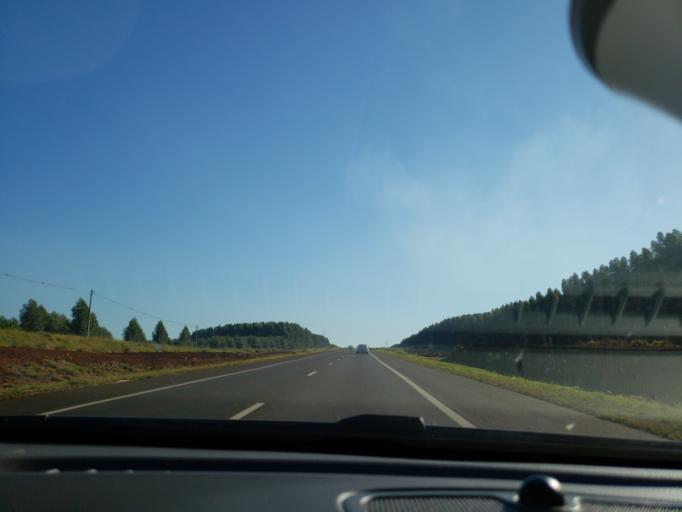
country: AR
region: Misiones
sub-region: Departamento de Capital
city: Posadas
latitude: -27.4654
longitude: -55.9386
